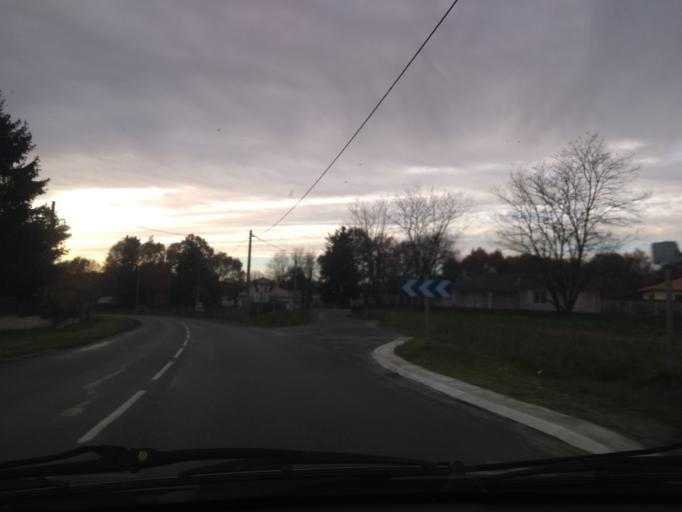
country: FR
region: Aquitaine
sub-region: Departement de la Gironde
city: Saucats
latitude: 44.6515
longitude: -0.6056
